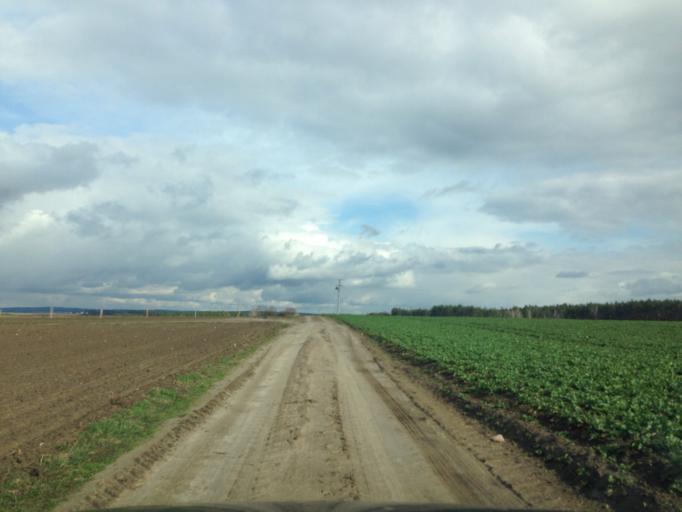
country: PL
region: Kujawsko-Pomorskie
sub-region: Powiat brodnicki
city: Bartniczka
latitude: 53.2487
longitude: 19.5813
